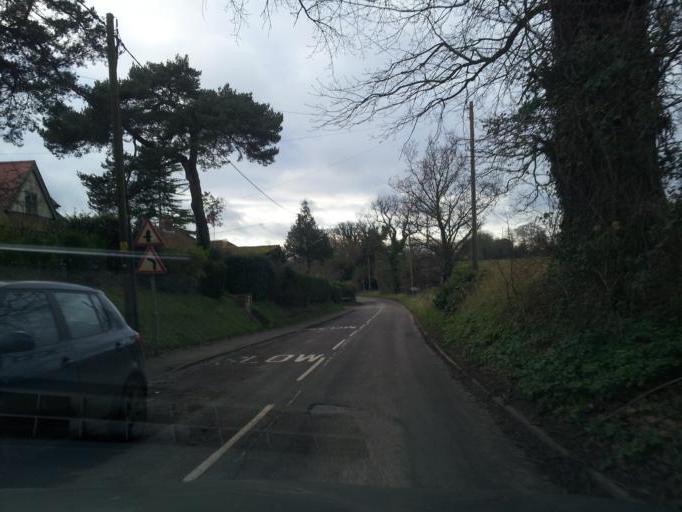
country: GB
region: England
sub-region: Norfolk
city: Brundall
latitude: 52.6255
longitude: 1.4189
